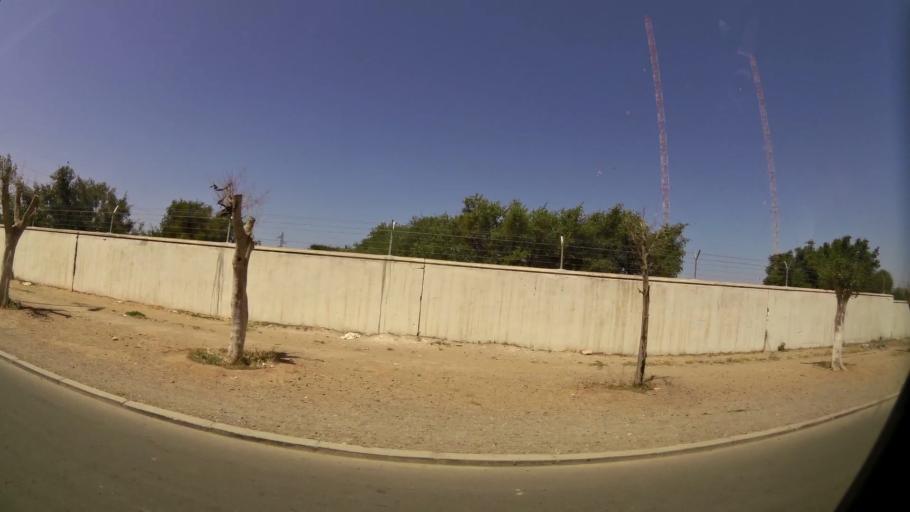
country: MA
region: Souss-Massa-Draa
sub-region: Inezgane-Ait Mellou
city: Inezgane
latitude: 30.3247
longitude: -9.5000
